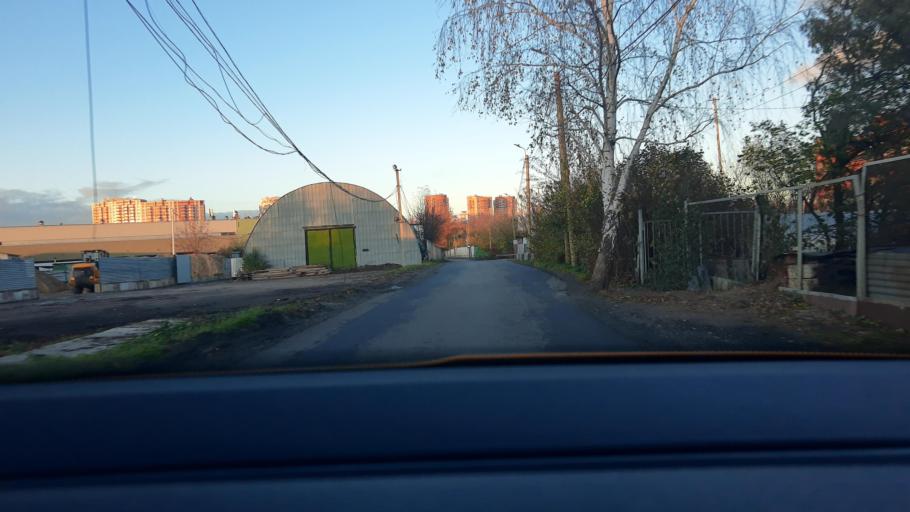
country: RU
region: Moscow
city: Strogino
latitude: 55.7862
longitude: 37.3968
